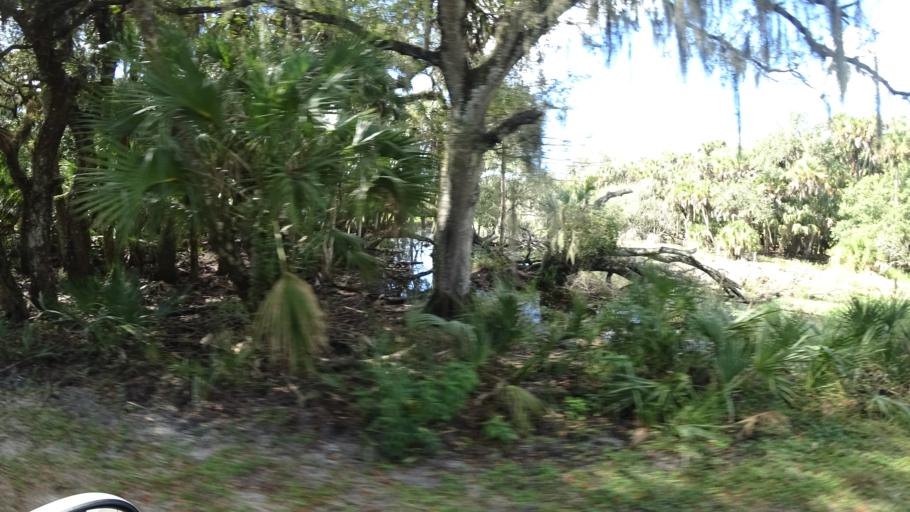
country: US
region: Florida
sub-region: Sarasota County
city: Lake Sarasota
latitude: 27.2647
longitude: -82.2859
